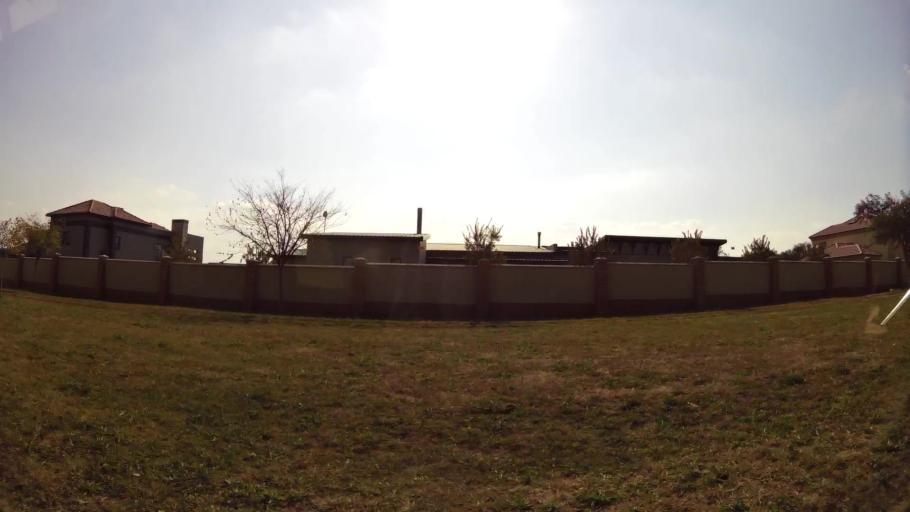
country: ZA
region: Gauteng
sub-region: City of Tshwane Metropolitan Municipality
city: Cullinan
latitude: -25.7805
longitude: 28.3850
